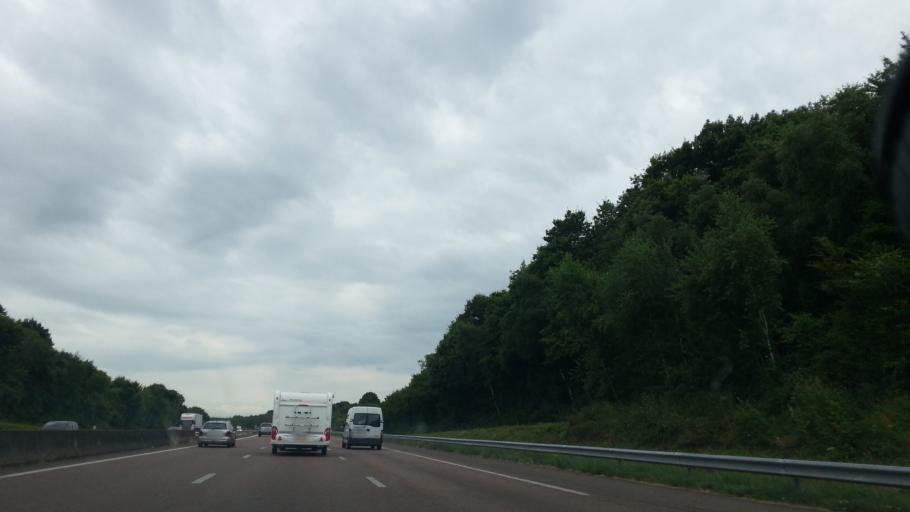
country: FR
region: Bourgogne
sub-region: Departement de Saone-et-Loire
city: Demigny
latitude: 46.8792
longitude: 4.8187
